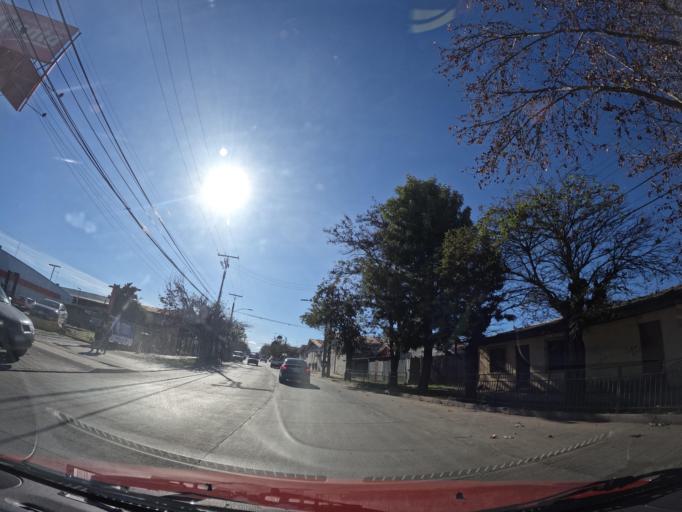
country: CL
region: Maule
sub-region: Provincia de Cauquenes
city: Cauquenes
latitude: -35.9726
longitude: -72.3149
